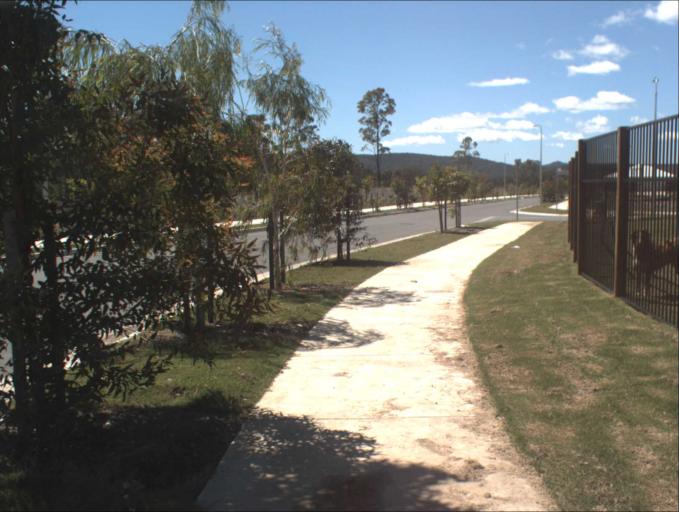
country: AU
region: Queensland
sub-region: Logan
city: Chambers Flat
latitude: -27.7956
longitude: 153.1043
